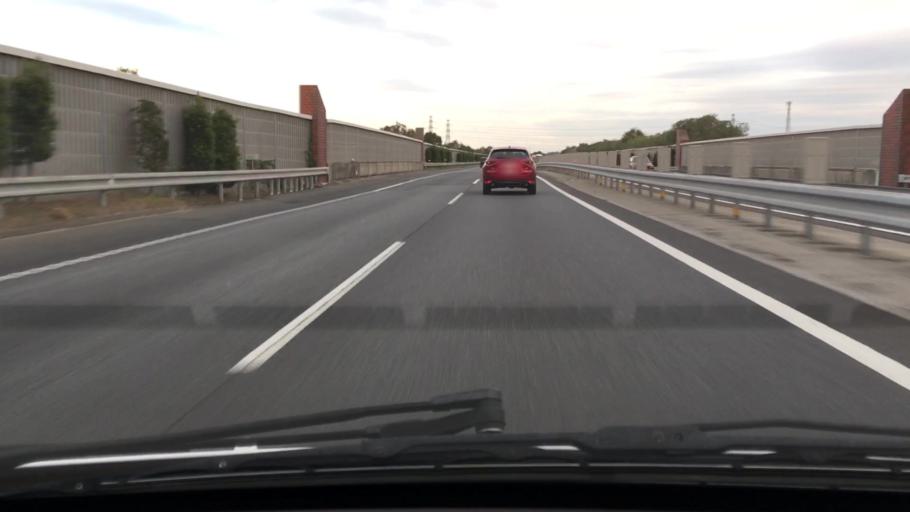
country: JP
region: Chiba
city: Ichihara
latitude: 35.5027
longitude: 140.1008
